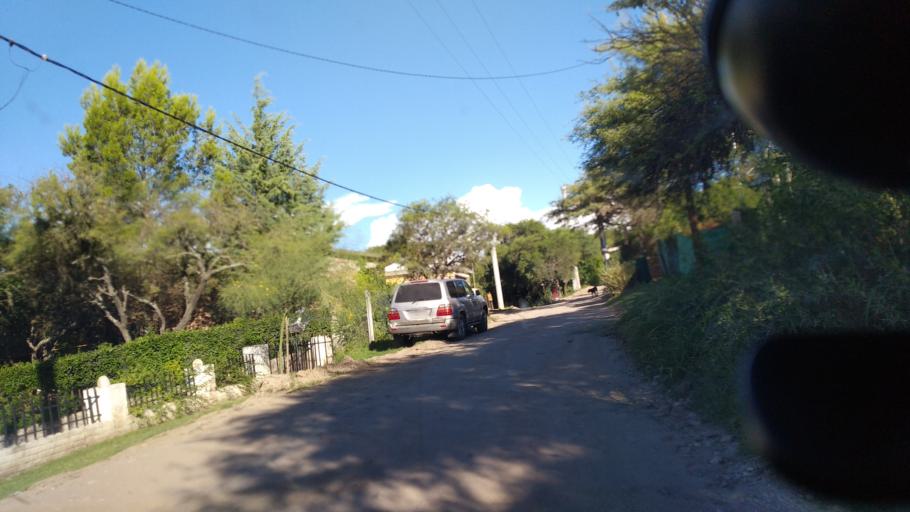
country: AR
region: Cordoba
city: Mina Clavero
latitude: -31.7272
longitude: -64.9967
